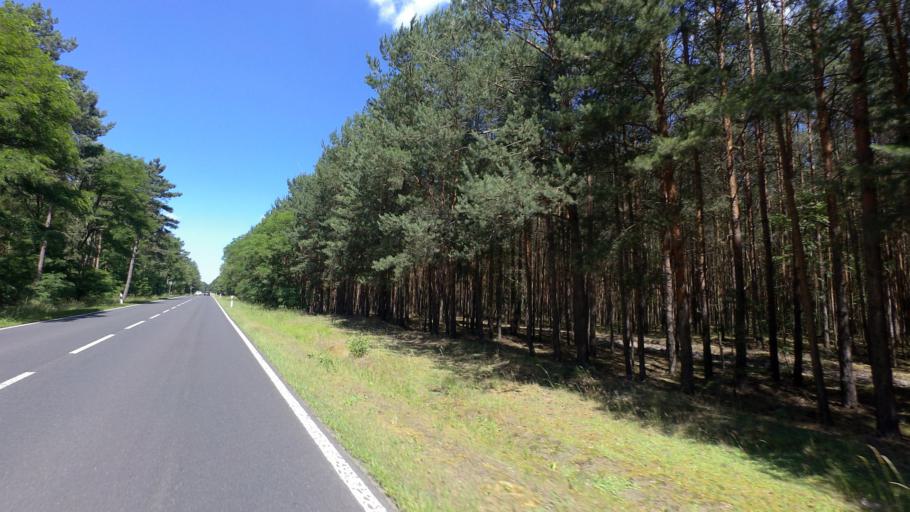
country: DE
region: Brandenburg
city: Baruth
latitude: 52.0090
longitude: 13.5515
